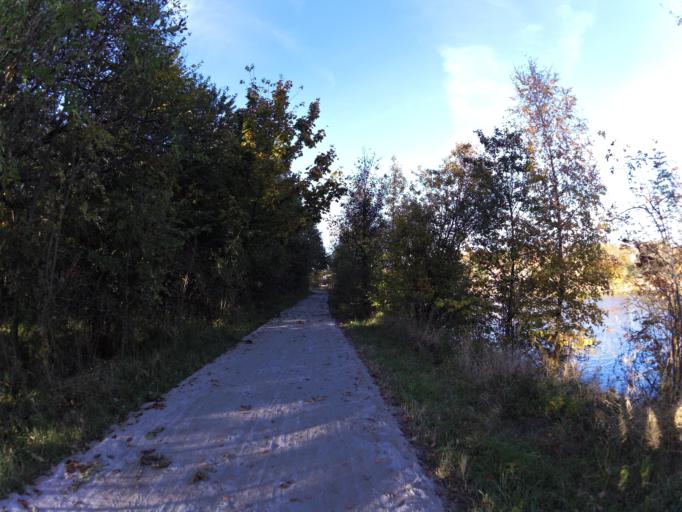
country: NO
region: Ostfold
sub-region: Sarpsborg
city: Sarpsborg
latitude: 59.2640
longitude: 11.1037
